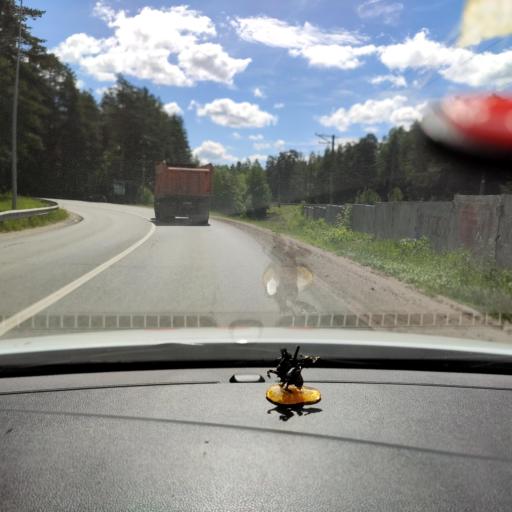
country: RU
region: Tatarstan
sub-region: Zelenodol'skiy Rayon
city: Vasil'yevo
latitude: 55.8462
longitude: 48.6806
